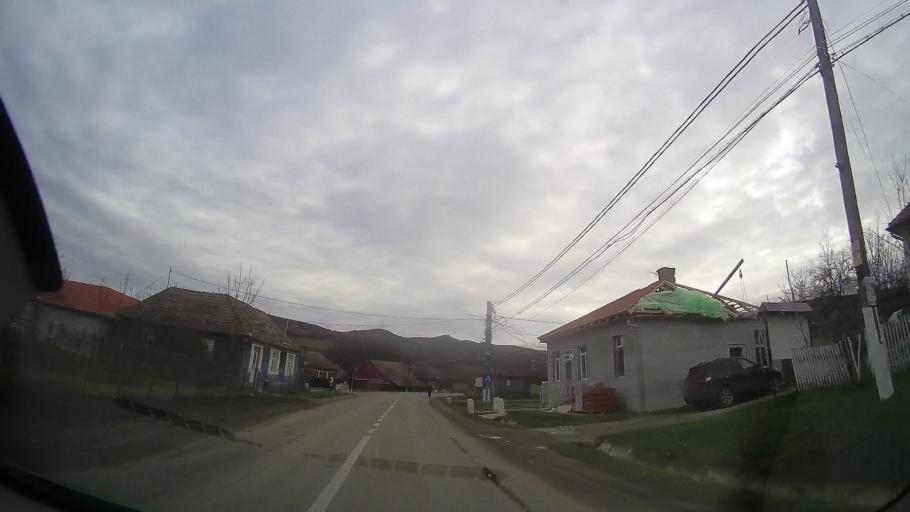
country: RO
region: Bistrita-Nasaud
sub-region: Comuna Budesti
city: Budesti
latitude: 46.8749
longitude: 24.2455
